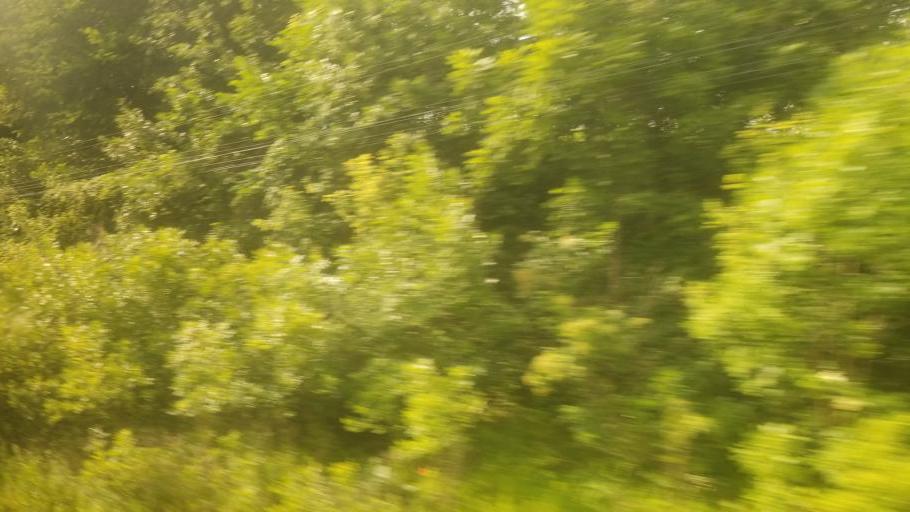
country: US
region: Kansas
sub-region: Douglas County
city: Lawrence
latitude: 39.0080
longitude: -95.2648
